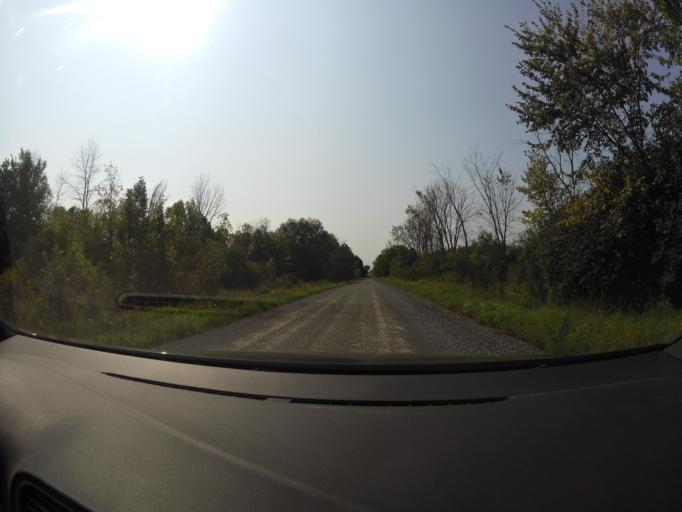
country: CA
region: Ontario
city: Arnprior
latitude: 45.4273
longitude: -76.2026
